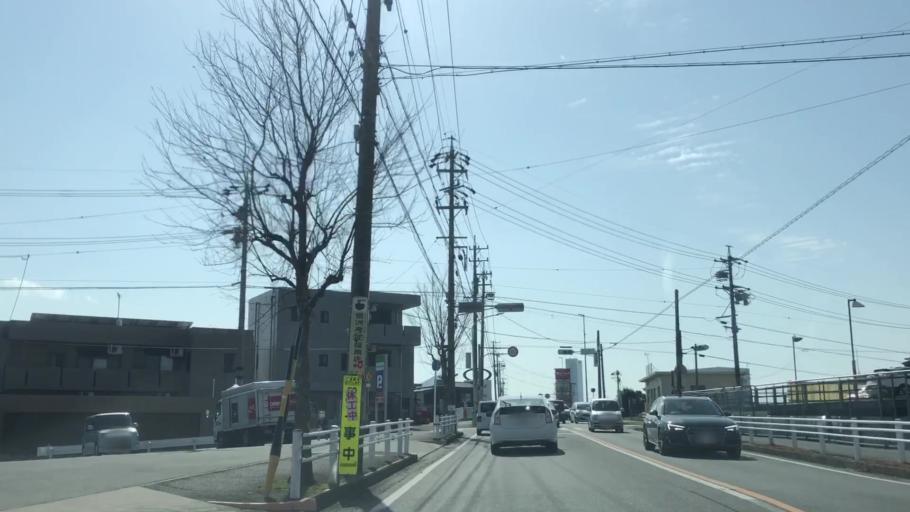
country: JP
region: Aichi
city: Toyohashi
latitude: 34.7538
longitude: 137.3794
